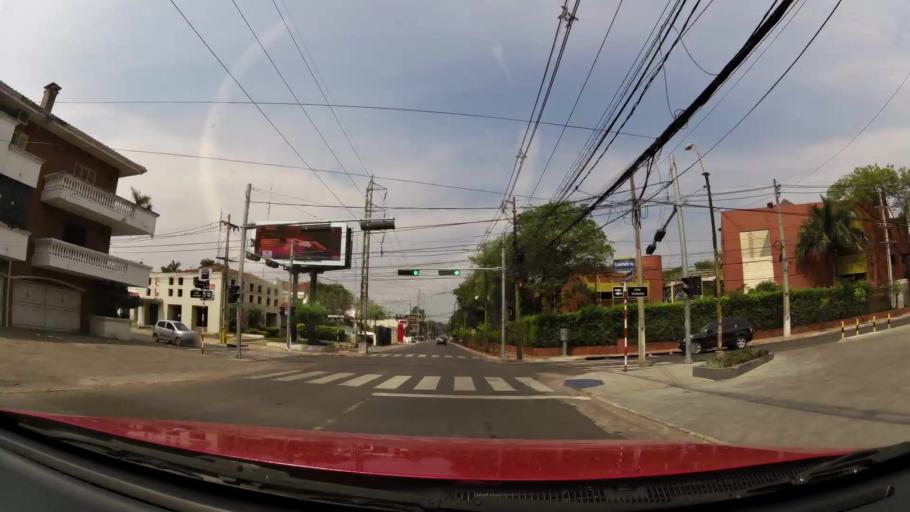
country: PY
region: Asuncion
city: Asuncion
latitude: -25.2872
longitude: -57.5951
